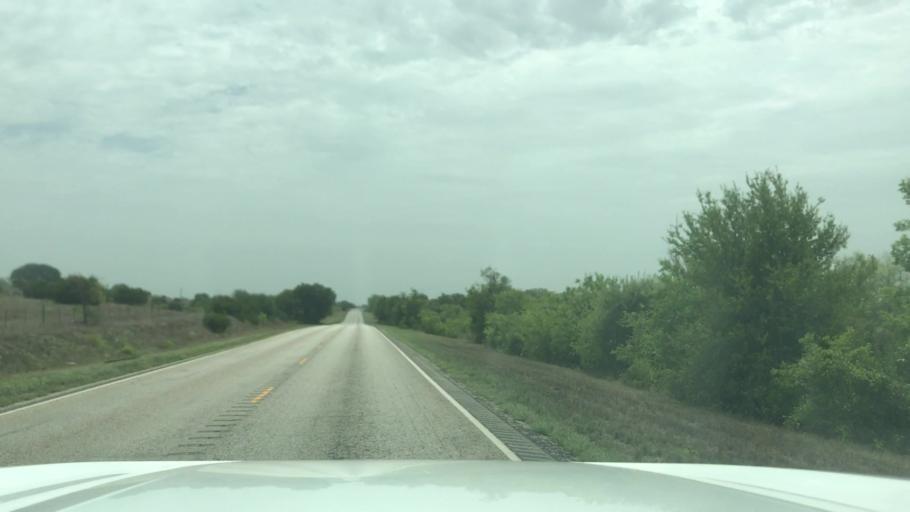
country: US
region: Texas
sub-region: Hamilton County
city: Hico
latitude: 32.0496
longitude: -98.1586
